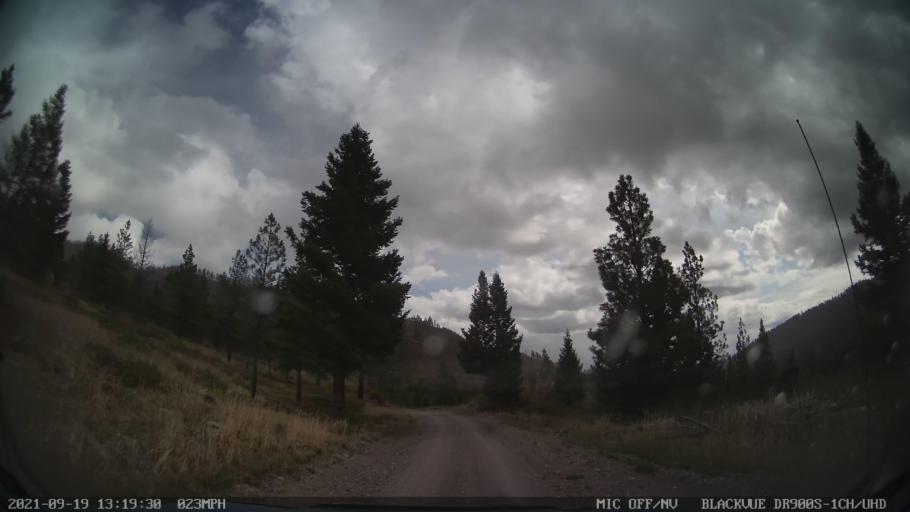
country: US
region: Montana
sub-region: Missoula County
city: Seeley Lake
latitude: 47.1684
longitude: -113.3486
